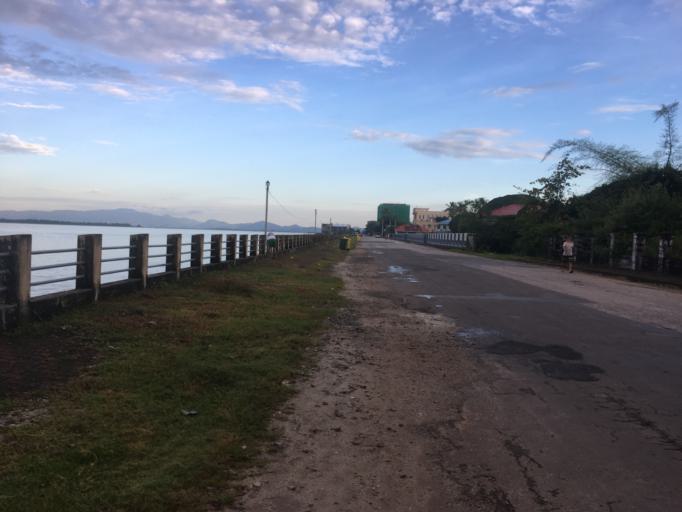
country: MM
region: Mon
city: Mawlamyine
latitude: 16.4666
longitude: 97.6220
